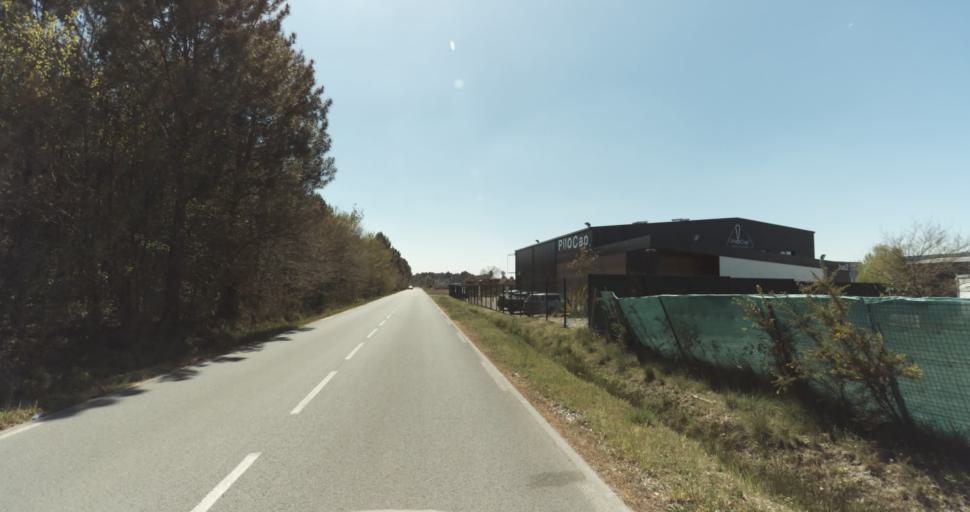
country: FR
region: Aquitaine
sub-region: Departement de la Gironde
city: Martignas-sur-Jalle
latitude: 44.8087
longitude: -0.7522
